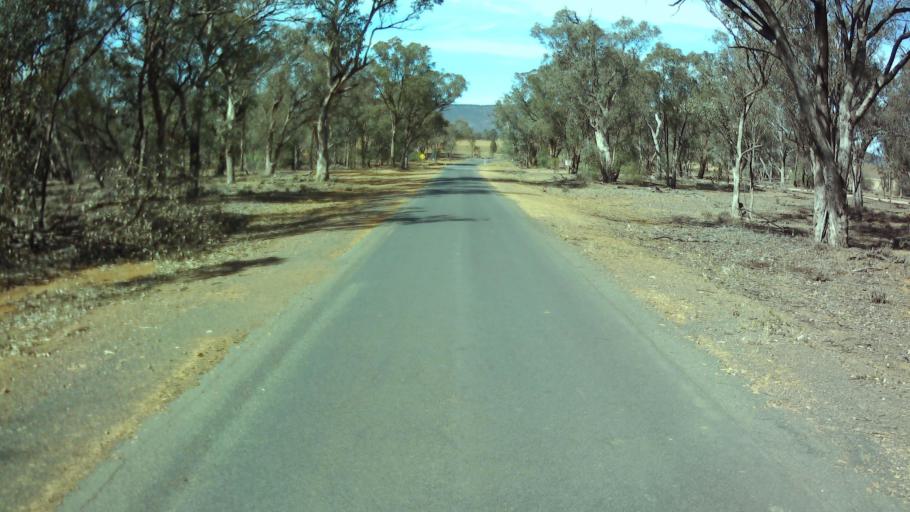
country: AU
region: New South Wales
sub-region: Weddin
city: Grenfell
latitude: -33.9385
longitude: 148.0799
